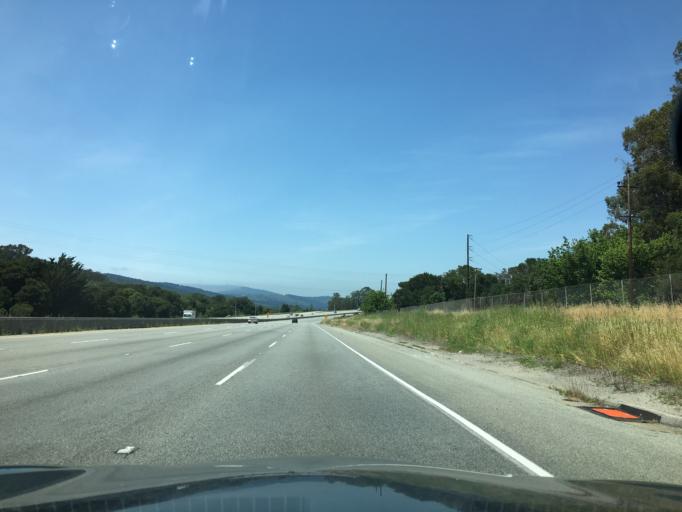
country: US
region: California
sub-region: San Mateo County
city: Emerald Lake Hills
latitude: 37.4544
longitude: -122.2847
